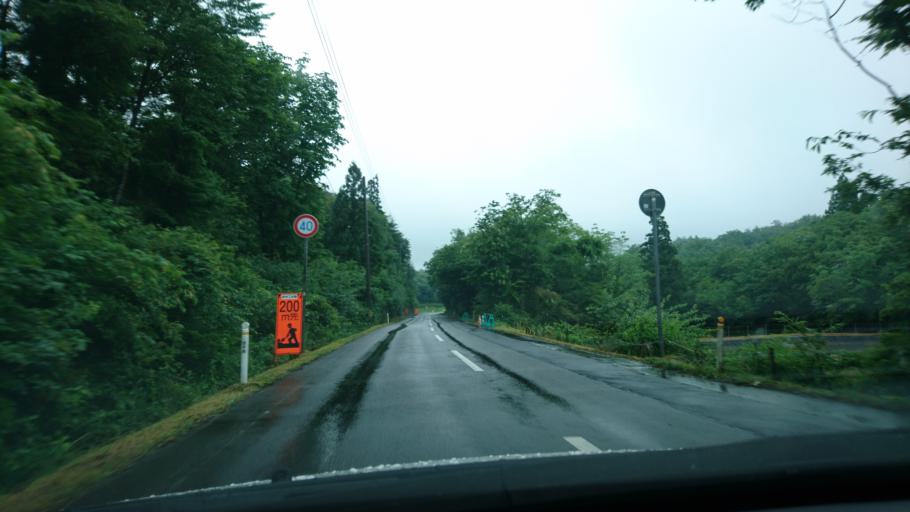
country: JP
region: Iwate
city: Ichinoseki
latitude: 38.9166
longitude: 141.0285
